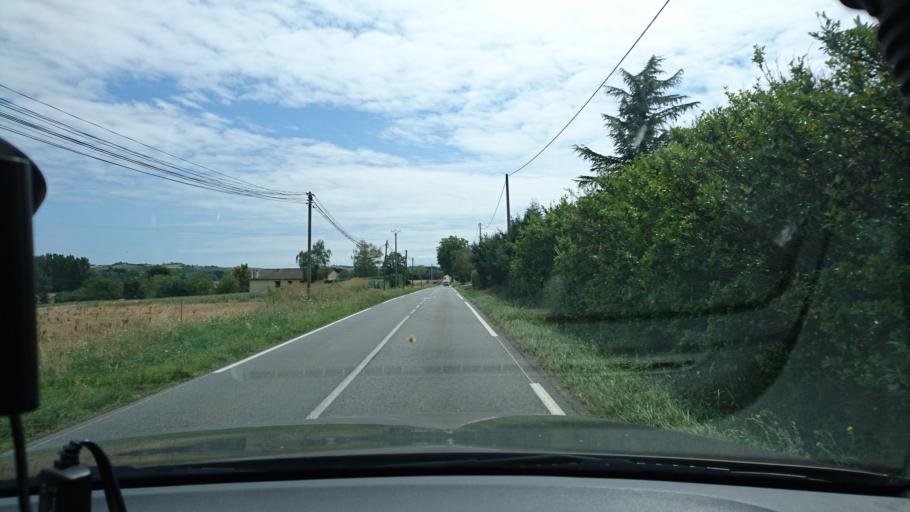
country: FR
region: Midi-Pyrenees
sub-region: Departement de la Haute-Garonne
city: Saint-Sulpice-sur-Leze
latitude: 43.3138
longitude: 1.3238
